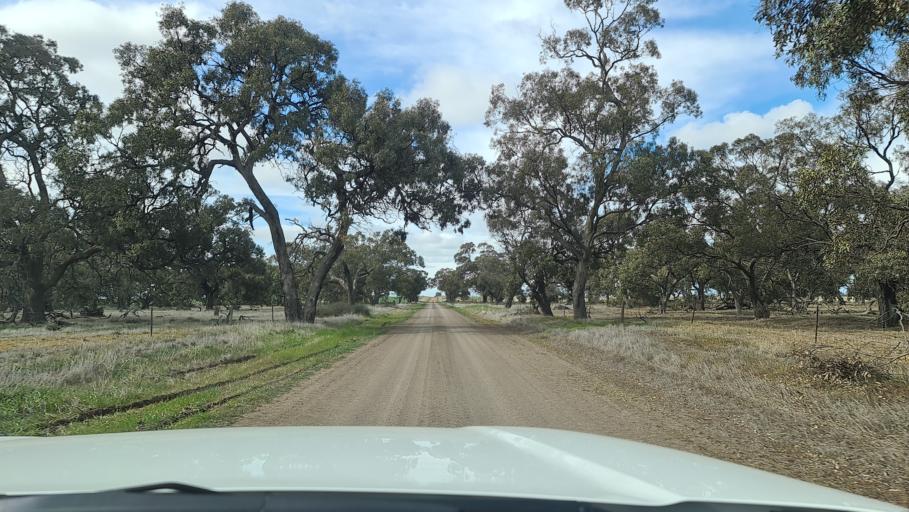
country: AU
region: Victoria
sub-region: Horsham
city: Horsham
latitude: -36.6313
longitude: 142.4135
